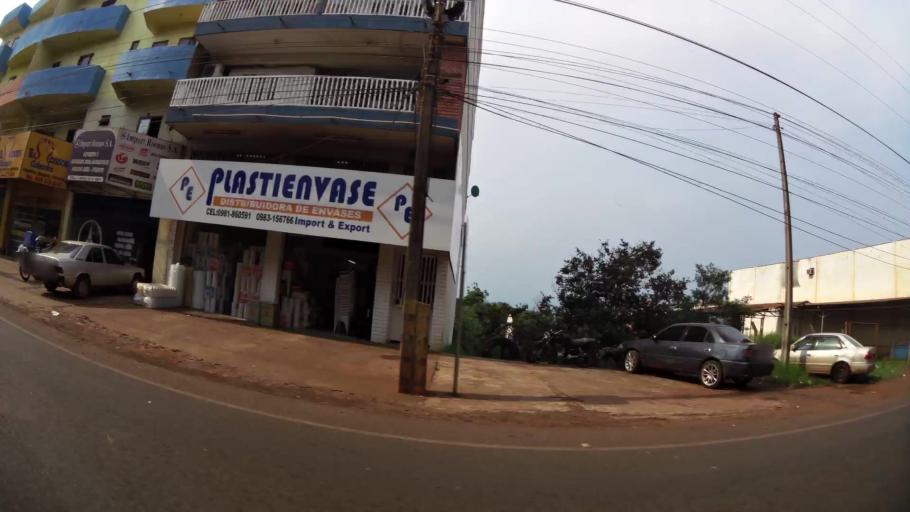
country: PY
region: Alto Parana
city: Ciudad del Este
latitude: -25.5045
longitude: -54.6457
